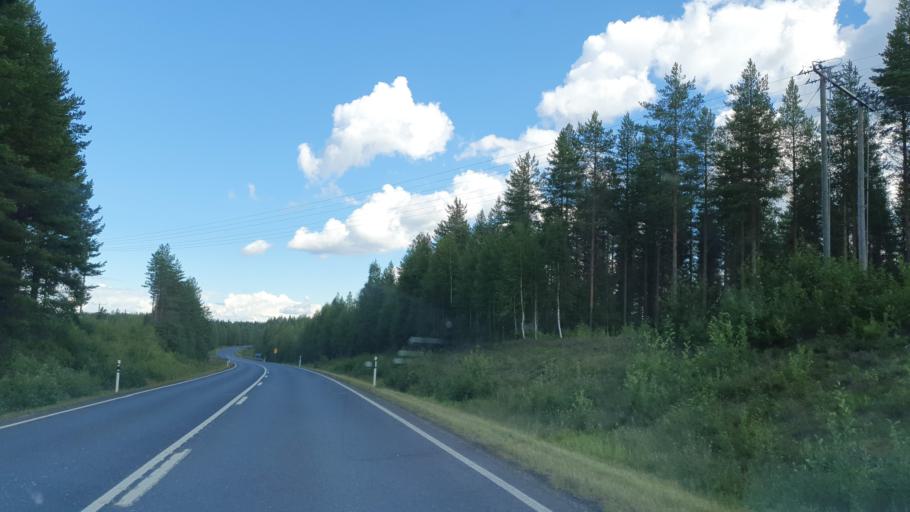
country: FI
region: North Karelia
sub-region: Pielisen Karjala
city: Valtimo
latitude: 64.0836
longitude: 28.9239
